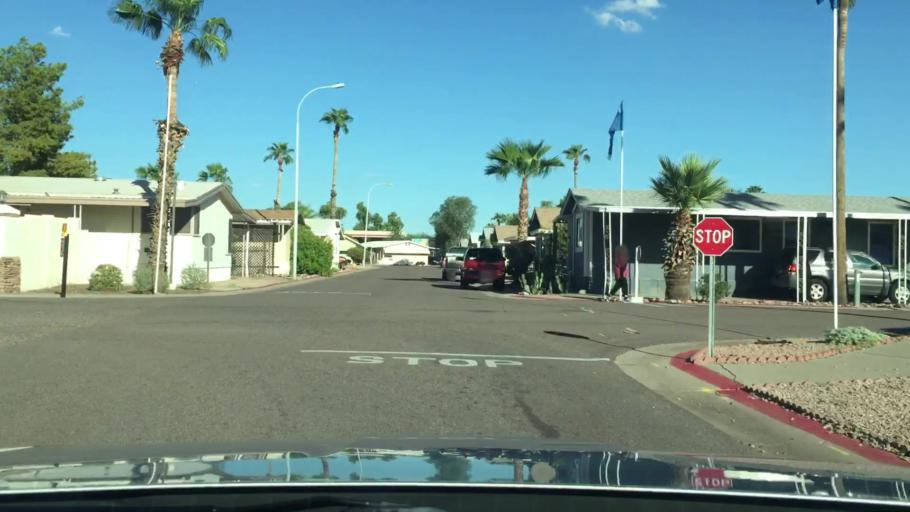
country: US
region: Arizona
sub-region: Maricopa County
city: Mesa
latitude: 33.4509
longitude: -111.8448
